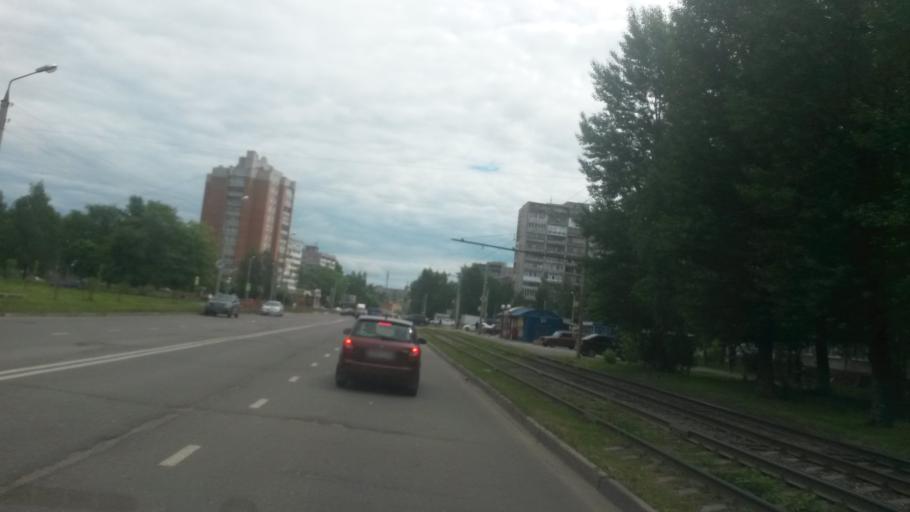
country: RU
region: Jaroslavl
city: Yaroslavl
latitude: 57.6810
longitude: 39.7771
